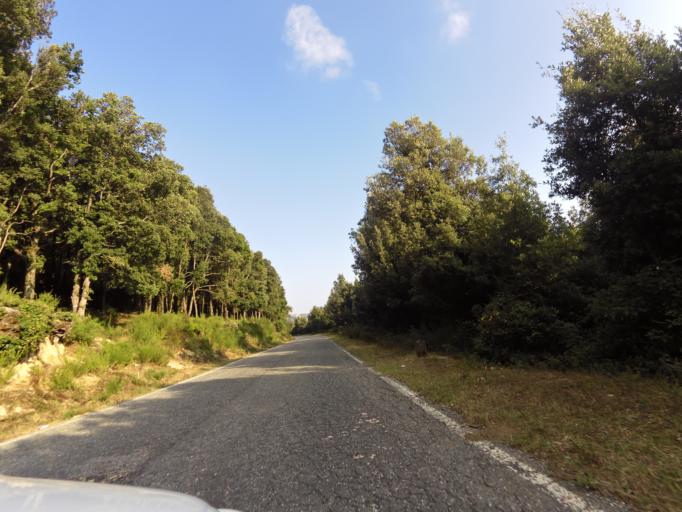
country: IT
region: Calabria
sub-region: Provincia di Reggio Calabria
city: Pazzano
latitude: 38.4752
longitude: 16.3997
